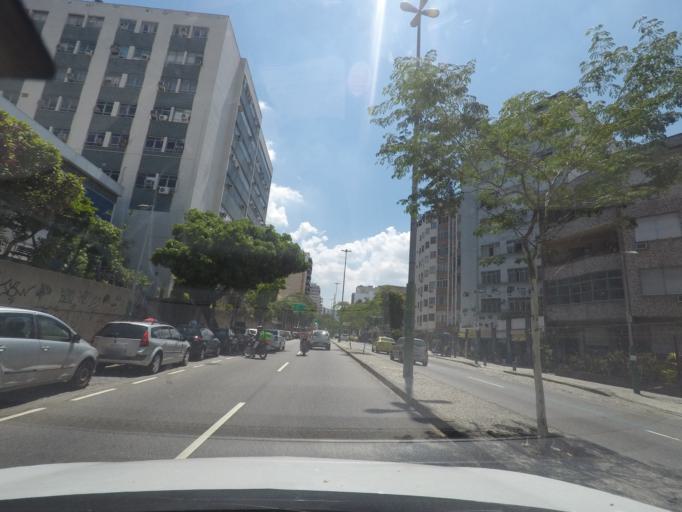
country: BR
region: Rio de Janeiro
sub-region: Rio De Janeiro
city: Rio de Janeiro
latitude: -22.9146
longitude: -43.2392
